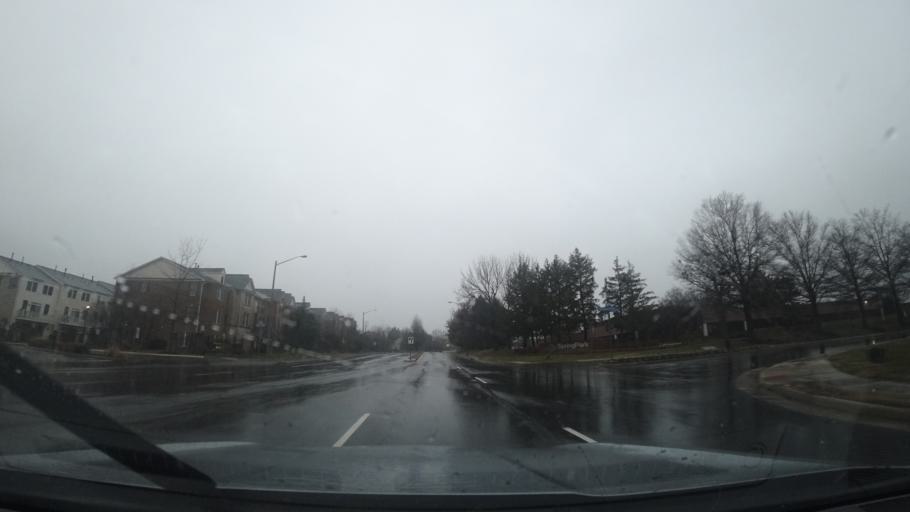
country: US
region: Virginia
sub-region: Fairfax County
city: Herndon
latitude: 38.9607
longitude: -77.3785
